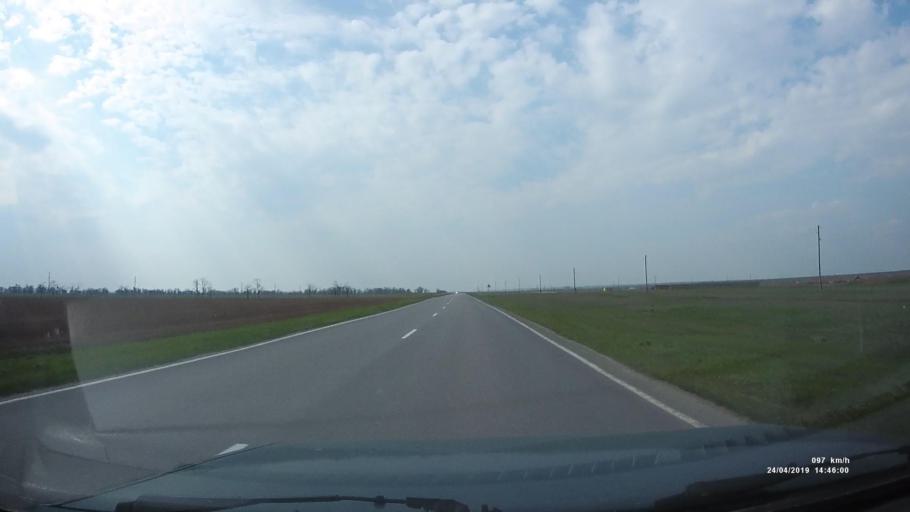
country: RU
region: Rostov
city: Remontnoye
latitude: 46.4780
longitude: 43.7975
